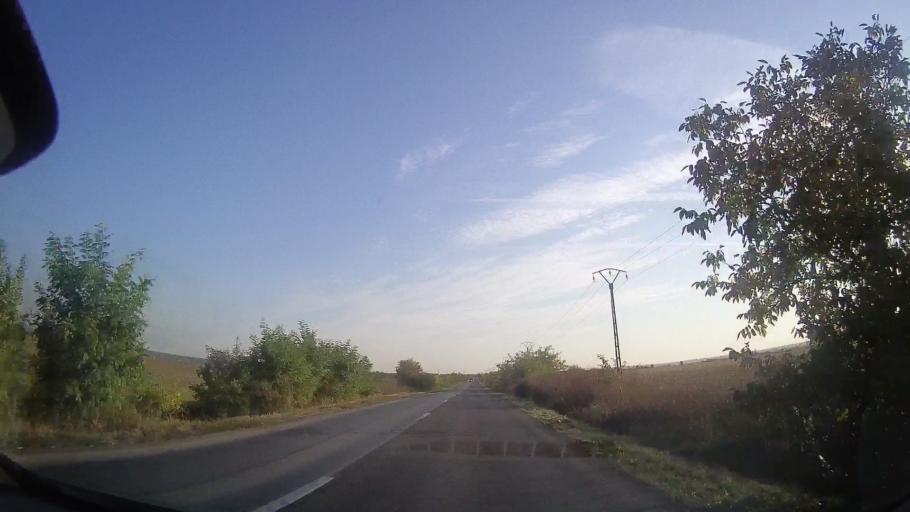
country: RO
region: Timis
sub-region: Comuna Pischia
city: Pischia
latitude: 45.8845
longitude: 21.3432
